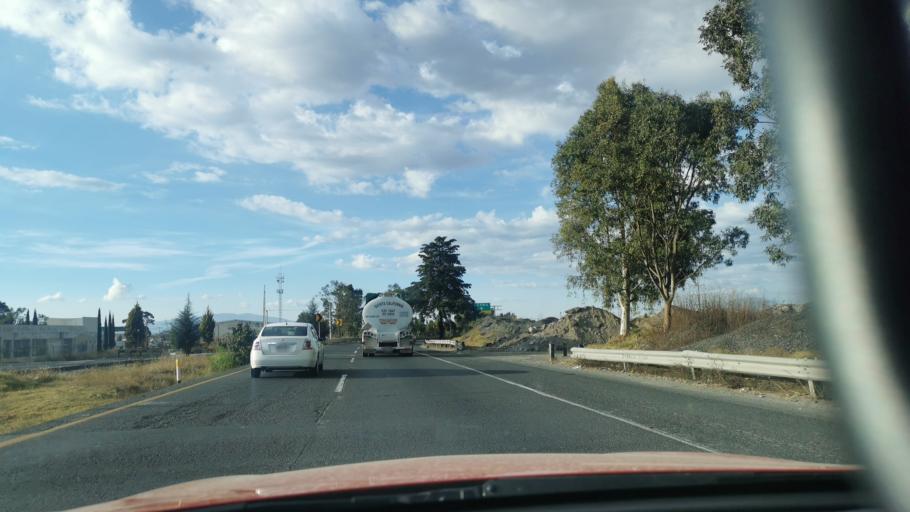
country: MX
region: Mexico
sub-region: Toluca
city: Colonia Aviacion Autopan
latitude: 19.3826
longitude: -99.7051
